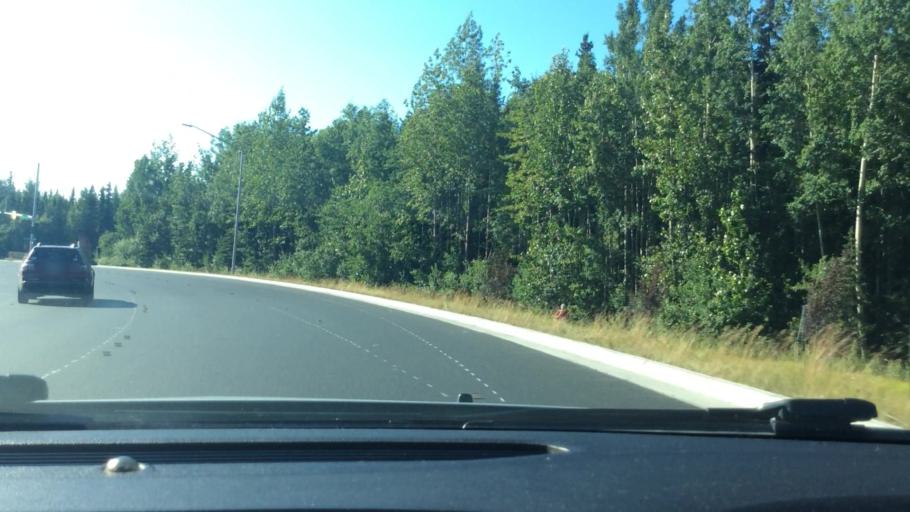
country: US
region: Alaska
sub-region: Anchorage Municipality
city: Elmendorf Air Force Base
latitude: 61.2305
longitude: -149.7347
